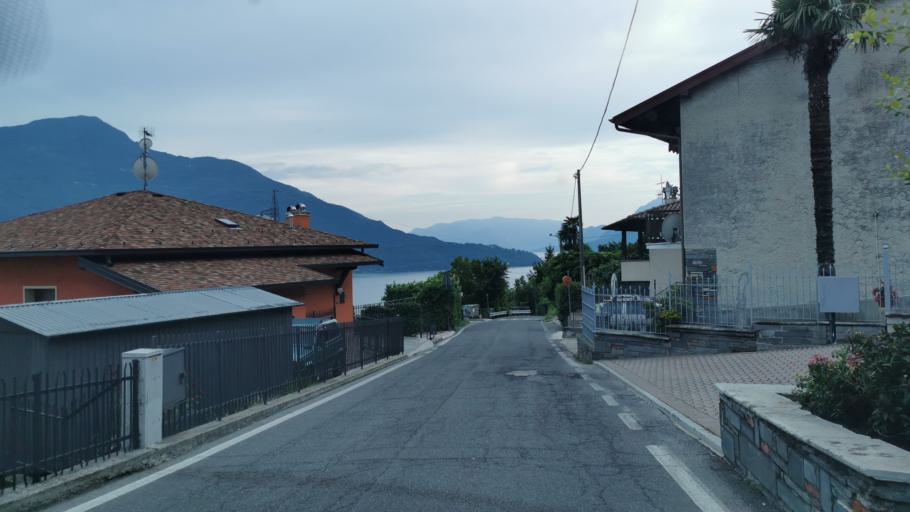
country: IT
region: Lombardy
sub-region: Provincia di Como
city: Vercana
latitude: 46.1598
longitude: 9.3382
